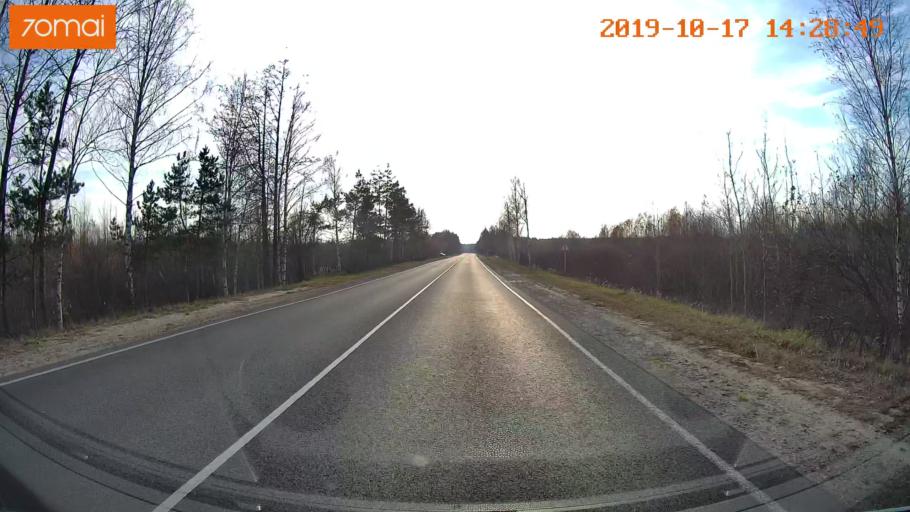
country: RU
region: Rjazan
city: Solotcha
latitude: 54.9683
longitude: 39.9500
